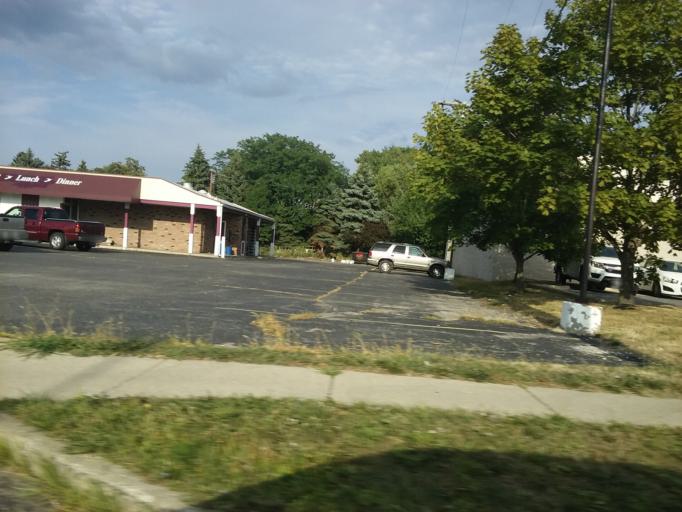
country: US
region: Ohio
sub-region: Wood County
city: Bowling Green
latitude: 41.3588
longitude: -83.6505
